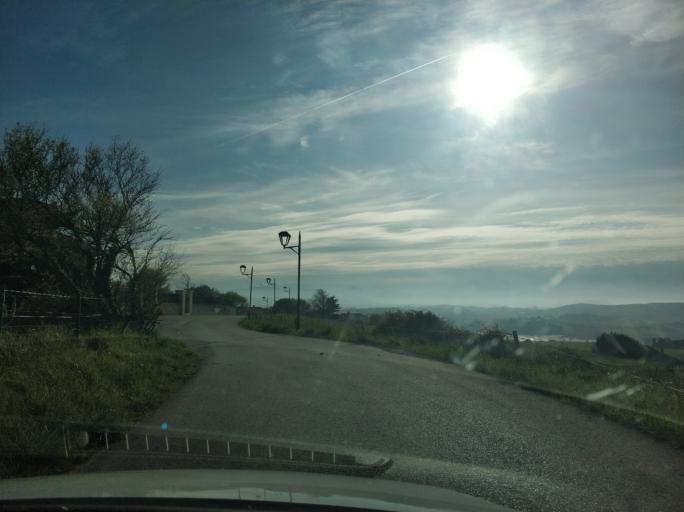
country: ES
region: Cantabria
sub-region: Provincia de Cantabria
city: Comillas
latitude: 43.3871
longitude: -4.3098
